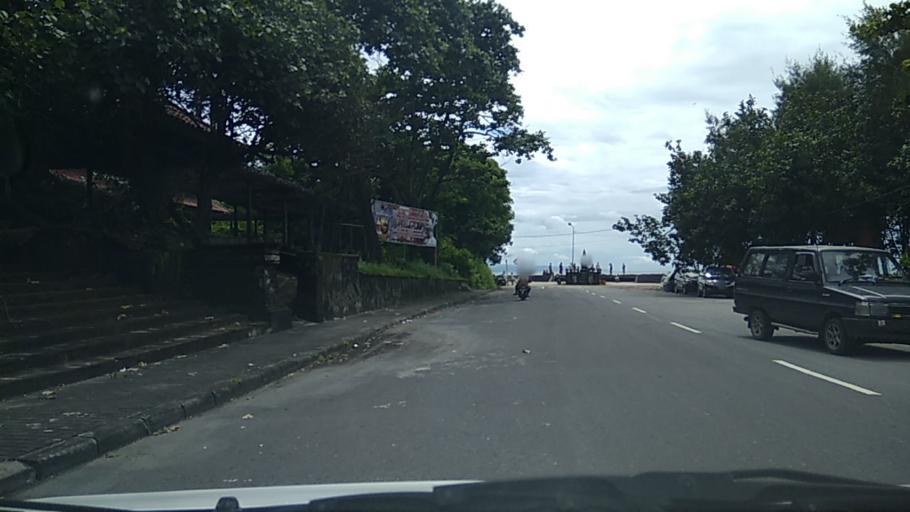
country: ID
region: Bali
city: Banjar Kertajiwa
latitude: -8.6578
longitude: 115.2647
